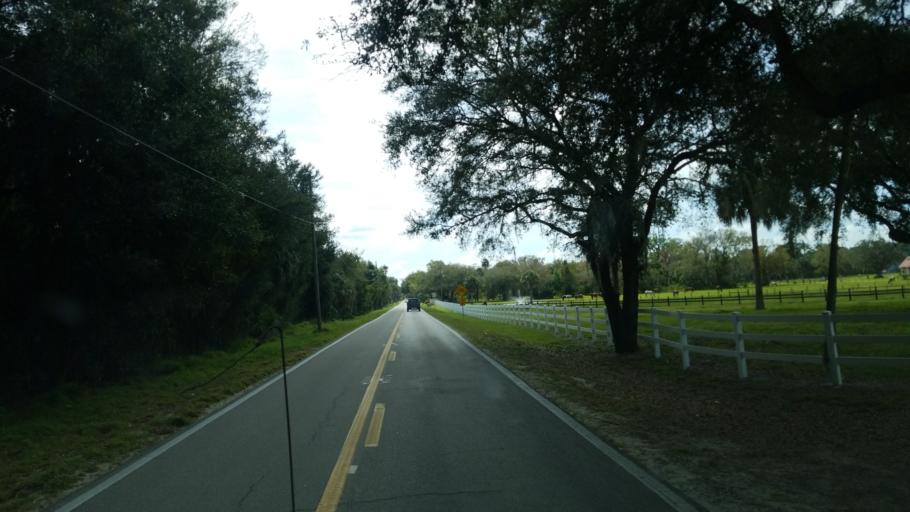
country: US
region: Florida
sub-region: Polk County
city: Dundee
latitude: 27.9957
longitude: -81.5500
